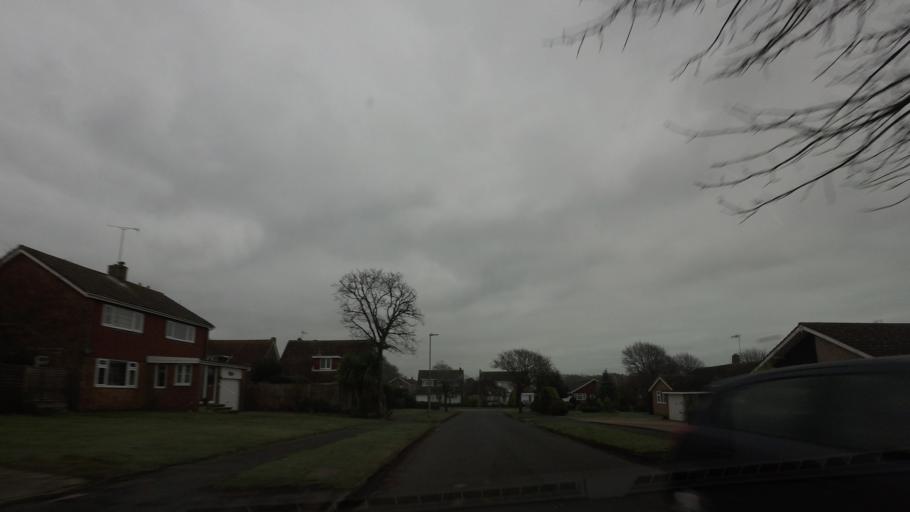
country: GB
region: England
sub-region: East Sussex
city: Bexhill-on-Sea
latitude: 50.8400
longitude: 0.4444
